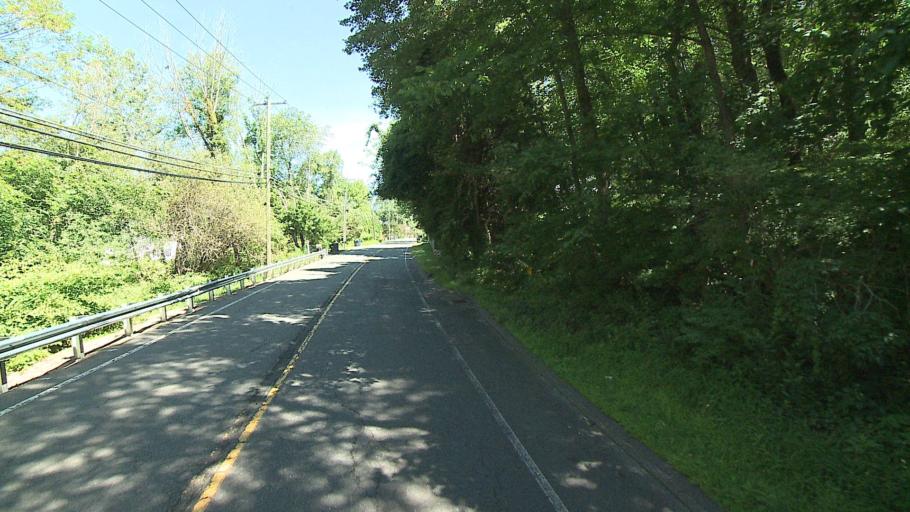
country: US
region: Connecticut
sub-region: Hartford County
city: Collinsville
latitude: 41.8420
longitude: -72.9257
